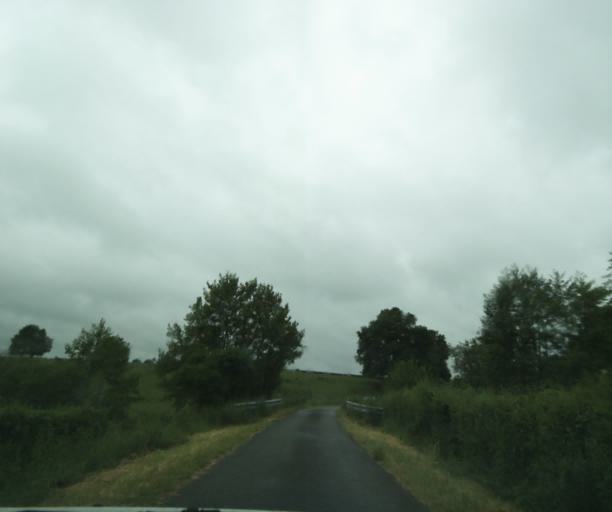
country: FR
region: Bourgogne
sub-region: Departement de Saone-et-Loire
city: Palinges
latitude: 46.4888
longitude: 4.1946
